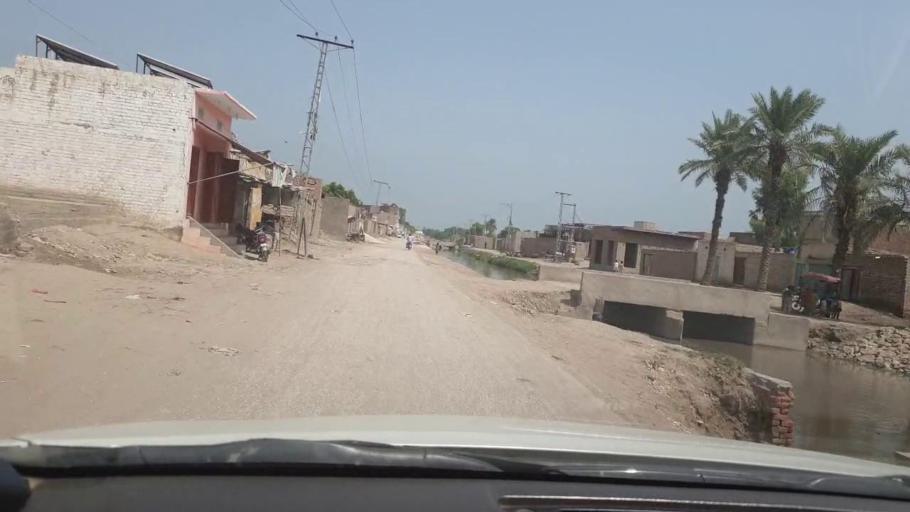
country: PK
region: Sindh
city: Shikarpur
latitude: 27.9451
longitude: 68.6327
